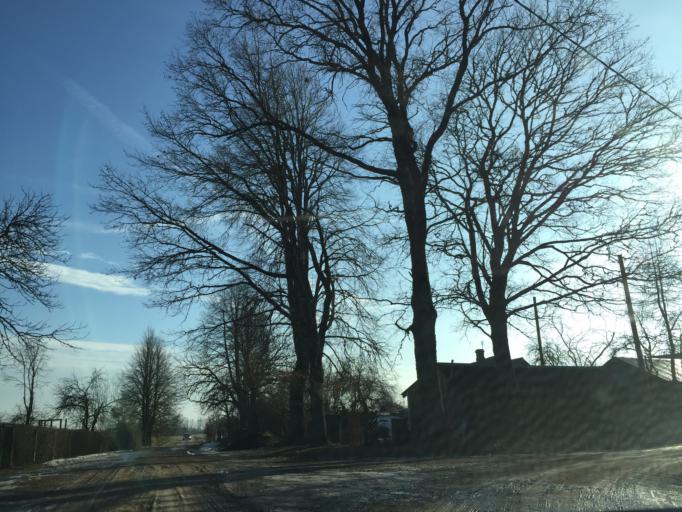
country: LV
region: Lecava
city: Iecava
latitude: 56.6812
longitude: 24.2048
